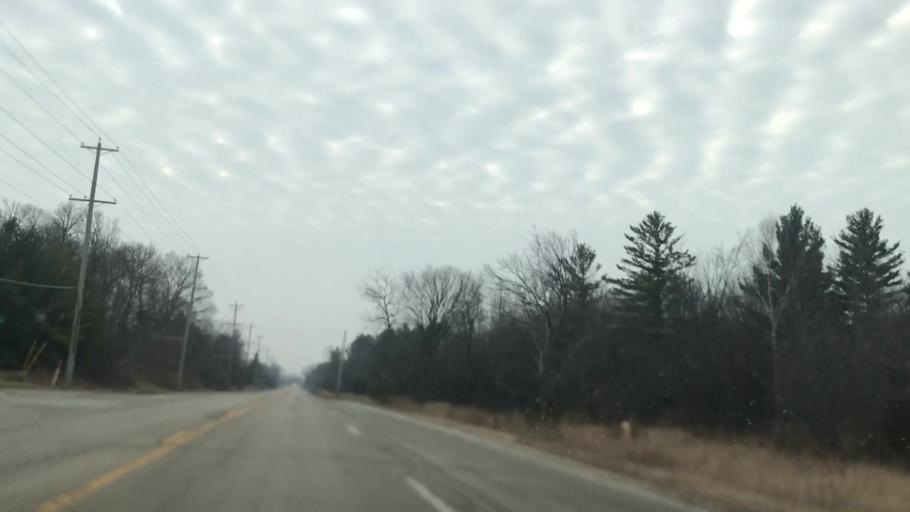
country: US
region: Wisconsin
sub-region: Ozaukee County
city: Cedarburg
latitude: 43.2881
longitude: -88.0041
